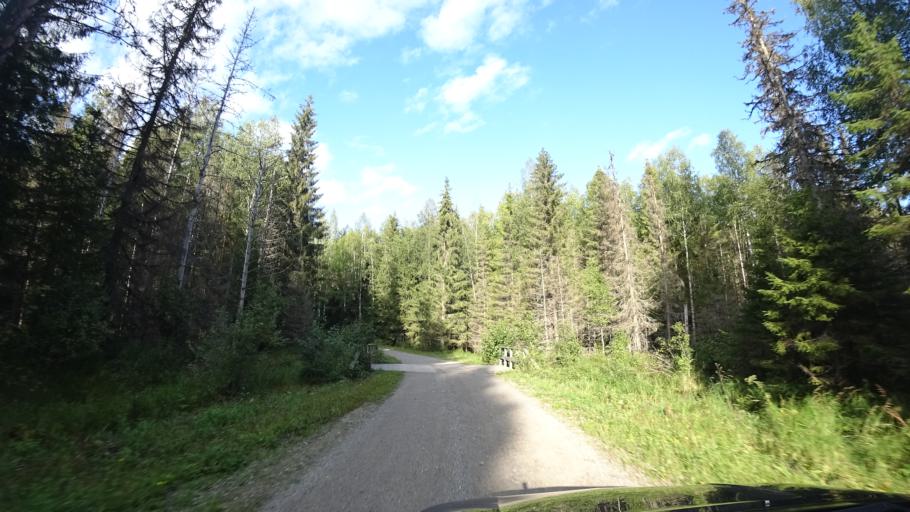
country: FI
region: Paijanne Tavastia
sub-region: Lahti
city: Auttoinen
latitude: 61.2156
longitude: 25.1760
